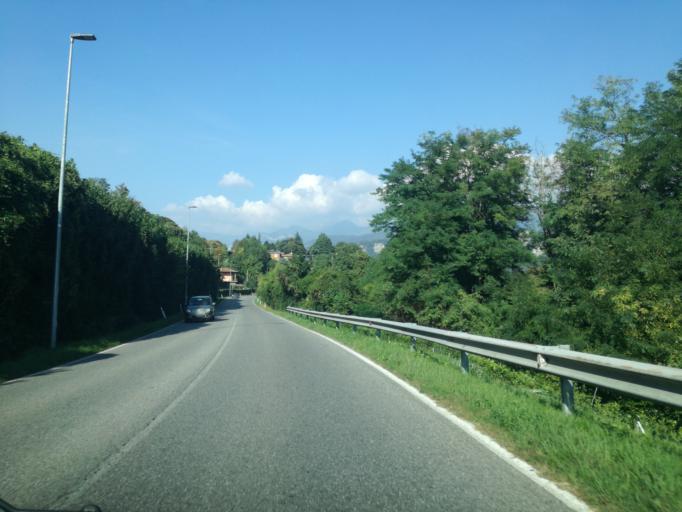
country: IT
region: Lombardy
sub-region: Provincia di Lecco
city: Brivio
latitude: 45.7334
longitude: 9.4438
